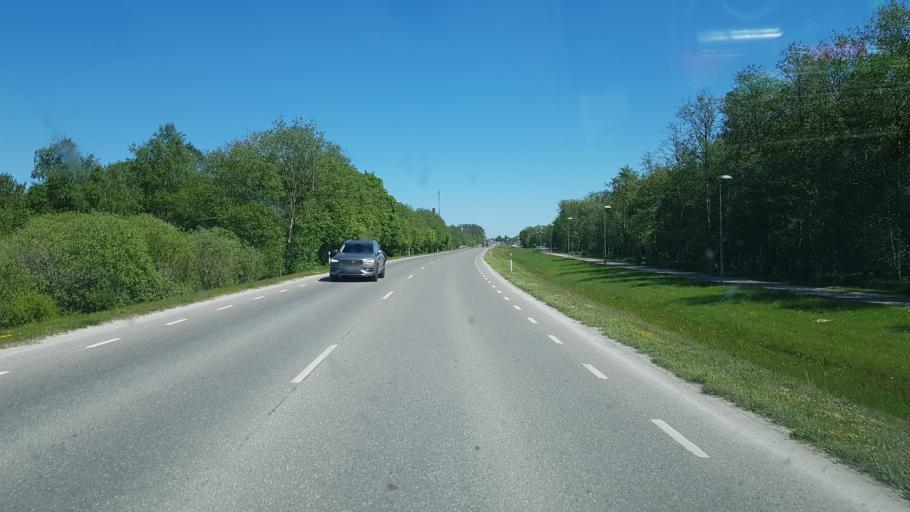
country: EE
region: Saare
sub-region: Kuressaare linn
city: Kuressaare
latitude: 58.2696
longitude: 22.4756
